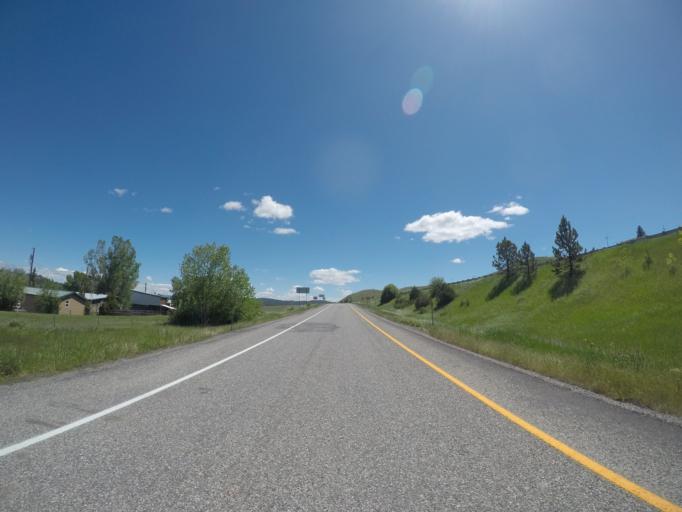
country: US
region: Montana
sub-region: Stillwater County
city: Absarokee
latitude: 45.7056
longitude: -109.5414
